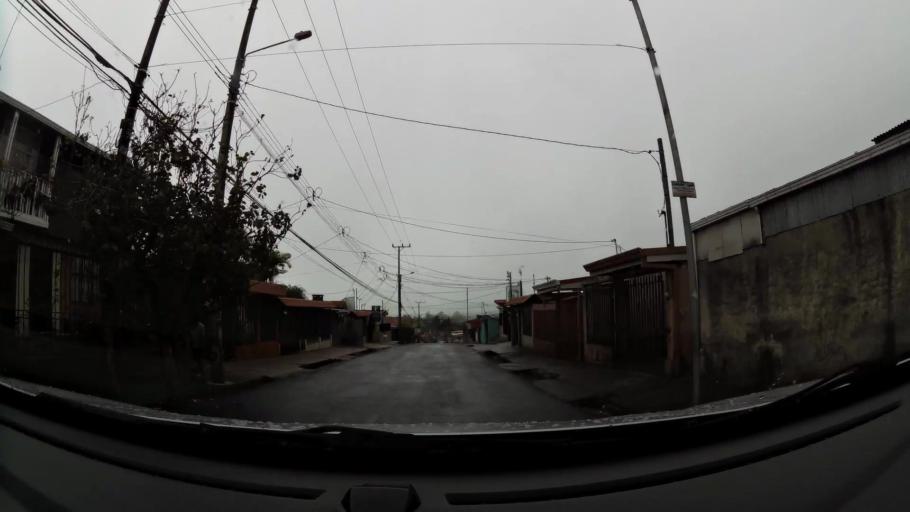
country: CR
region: Cartago
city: Paraiso
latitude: 9.8390
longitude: -83.8646
